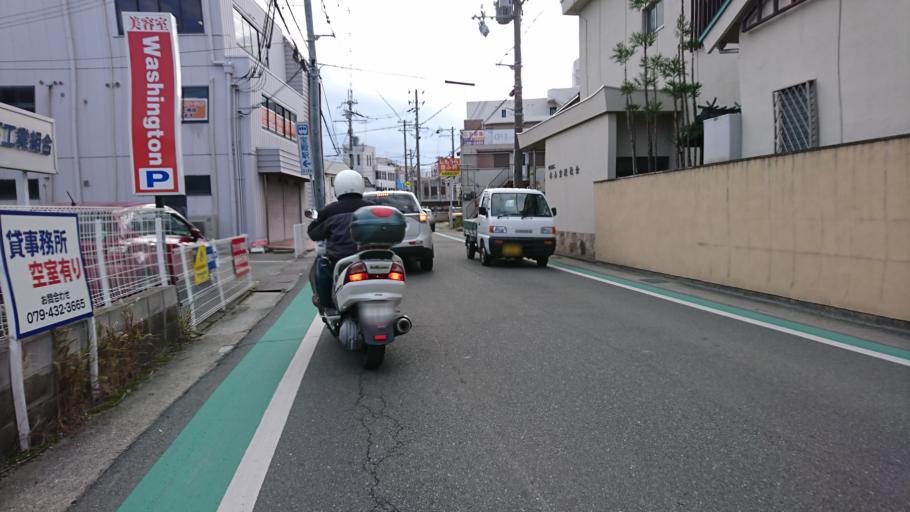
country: JP
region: Hyogo
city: Kakogawacho-honmachi
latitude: 34.7865
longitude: 134.8103
